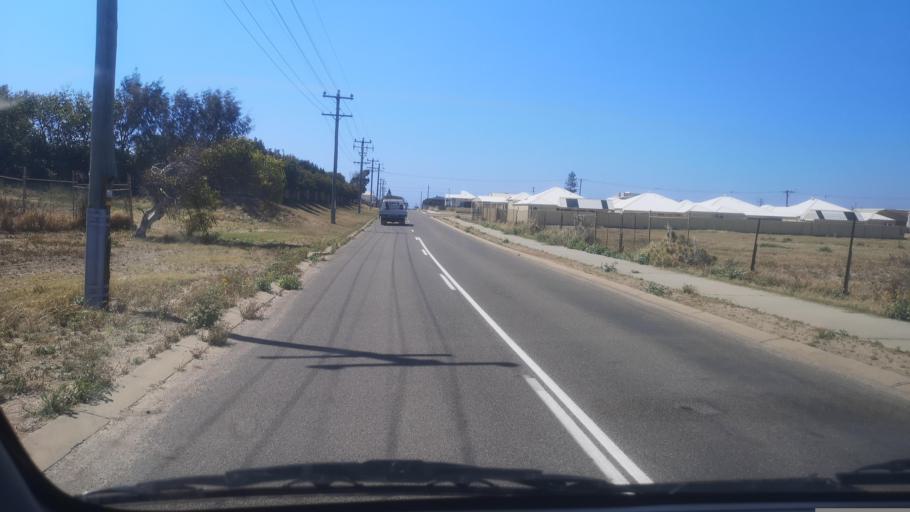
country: AU
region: Western Australia
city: Port Denison
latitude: -29.2793
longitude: 114.9195
